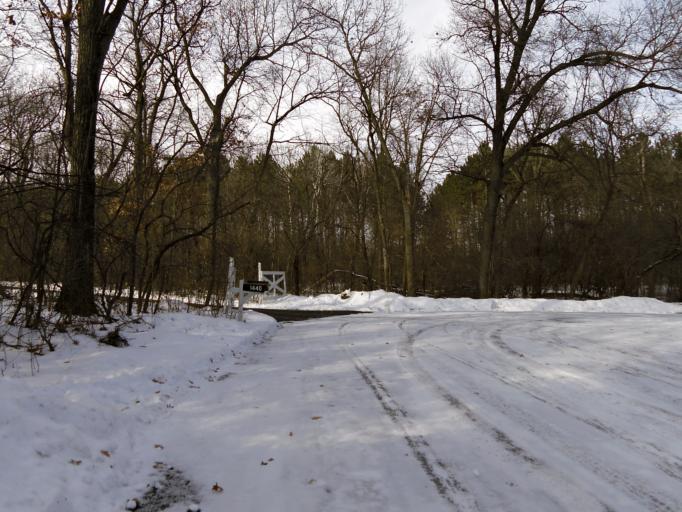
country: US
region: Minnesota
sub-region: Washington County
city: Lake Elmo
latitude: 44.9703
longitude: -92.8349
